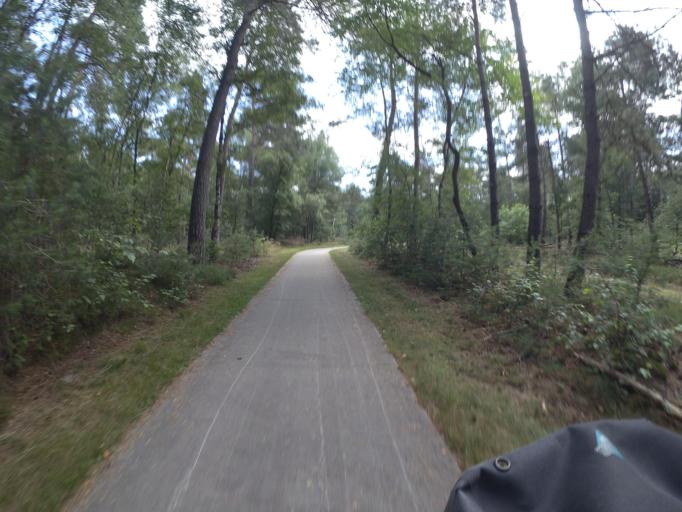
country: NL
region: Gelderland
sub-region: Gemeente Heerde
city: Heerde
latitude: 52.4253
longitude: 6.0303
